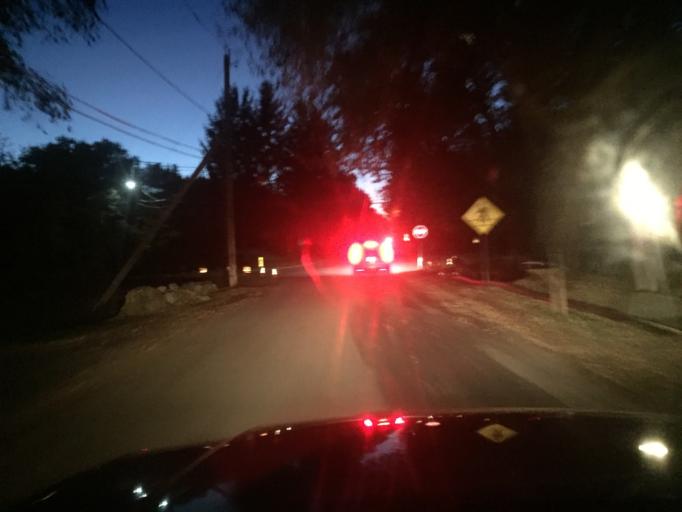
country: US
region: Massachusetts
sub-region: Norfolk County
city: Medway
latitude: 42.1572
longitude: -71.4082
